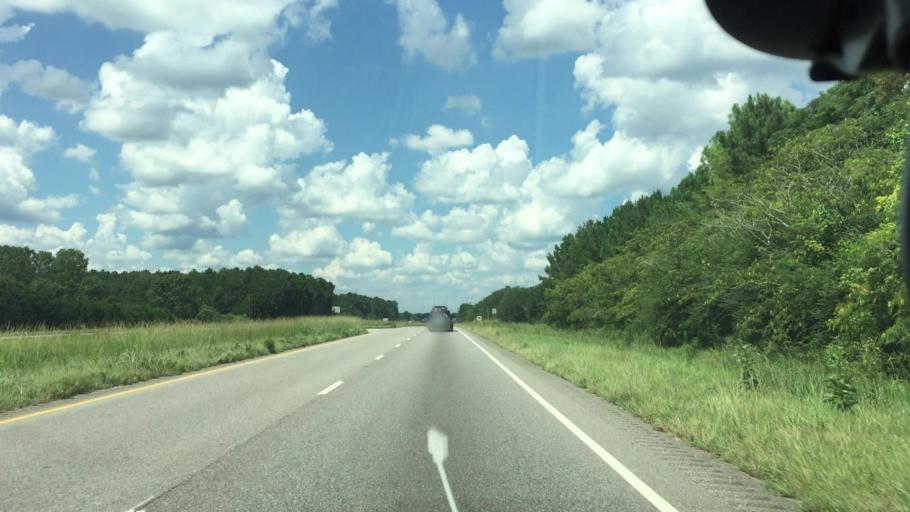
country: US
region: Alabama
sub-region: Montgomery County
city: Taylor
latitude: 32.0105
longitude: -86.0293
